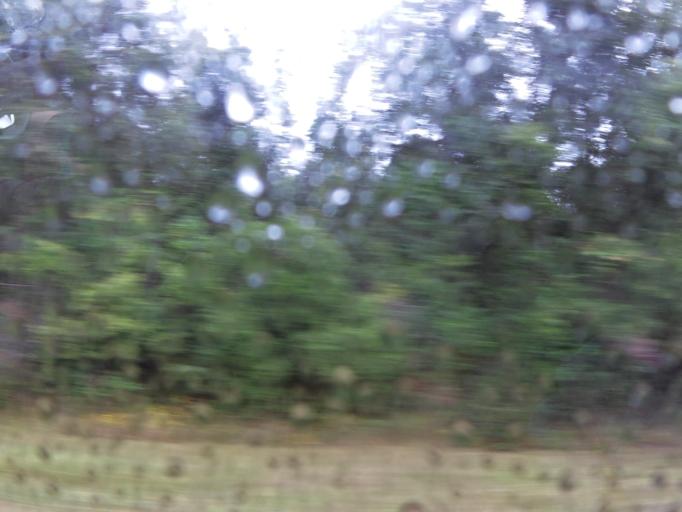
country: US
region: Florida
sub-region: Baker County
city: Macclenny
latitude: 30.3897
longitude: -82.1268
